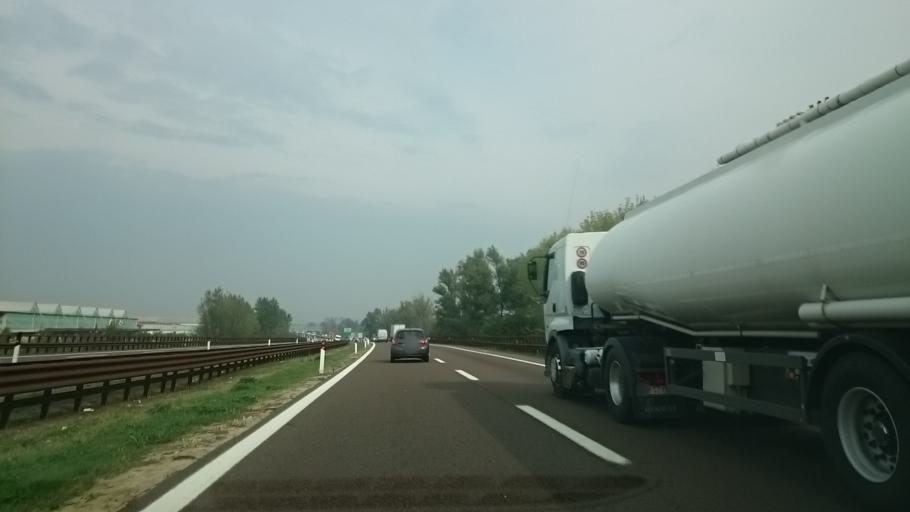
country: IT
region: Emilia-Romagna
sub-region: Provincia di Reggio Emilia
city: Rolo
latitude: 44.8902
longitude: 10.8507
